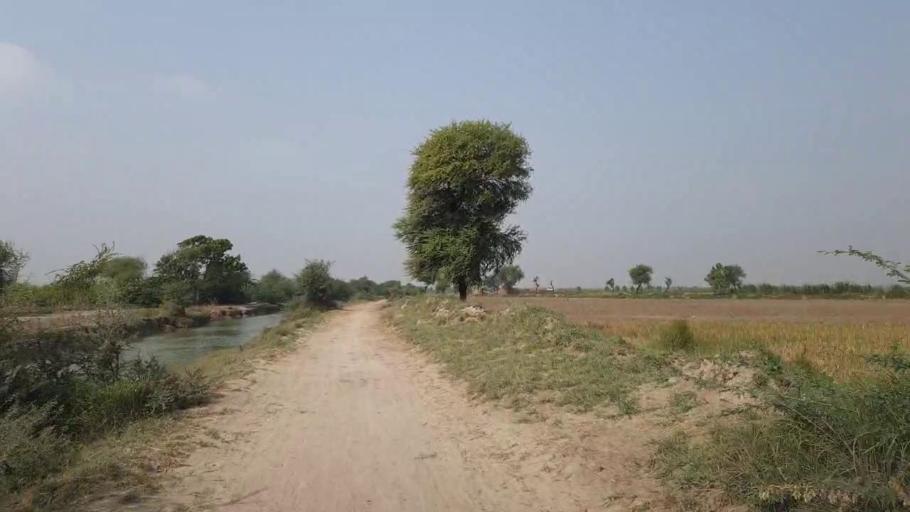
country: PK
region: Sindh
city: Kario
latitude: 24.8468
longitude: 68.5346
